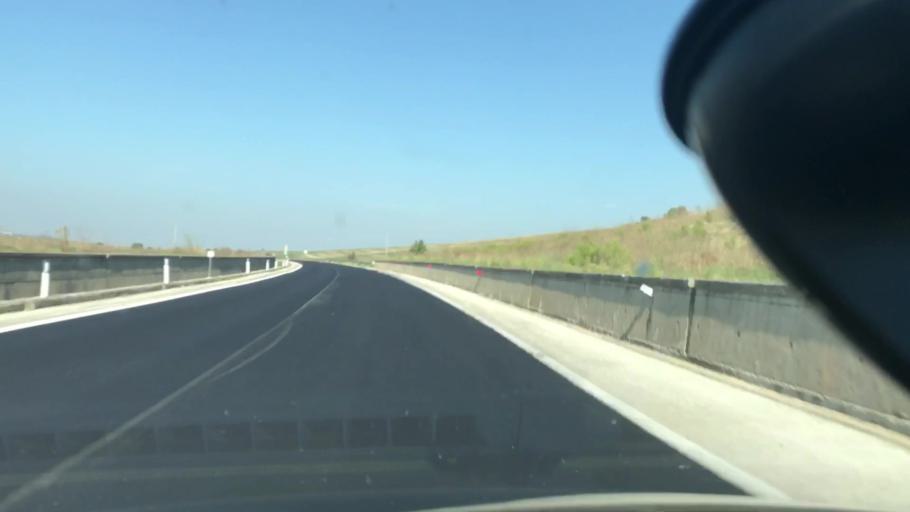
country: IT
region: Apulia
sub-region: Provincia di Barletta - Andria - Trani
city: Spinazzola
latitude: 40.9207
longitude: 16.0966
